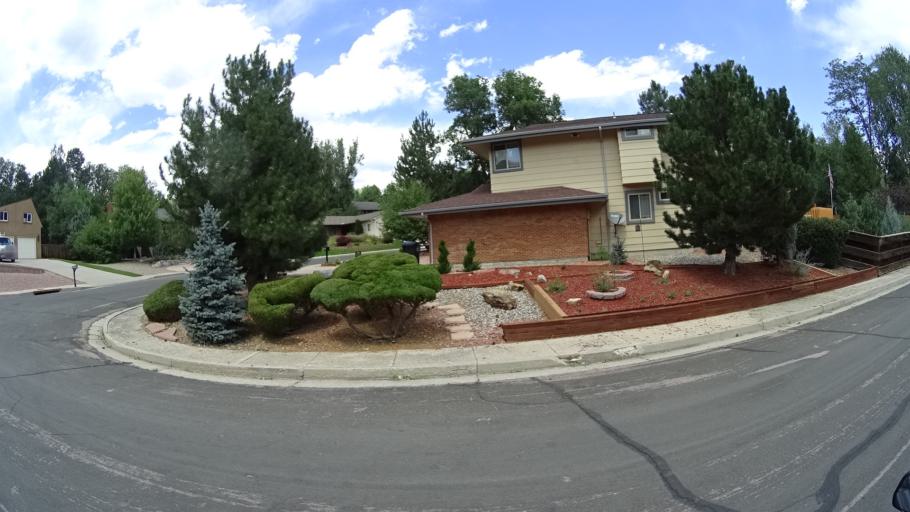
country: US
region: Colorado
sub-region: El Paso County
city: Stratmoor
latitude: 38.7828
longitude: -104.8285
